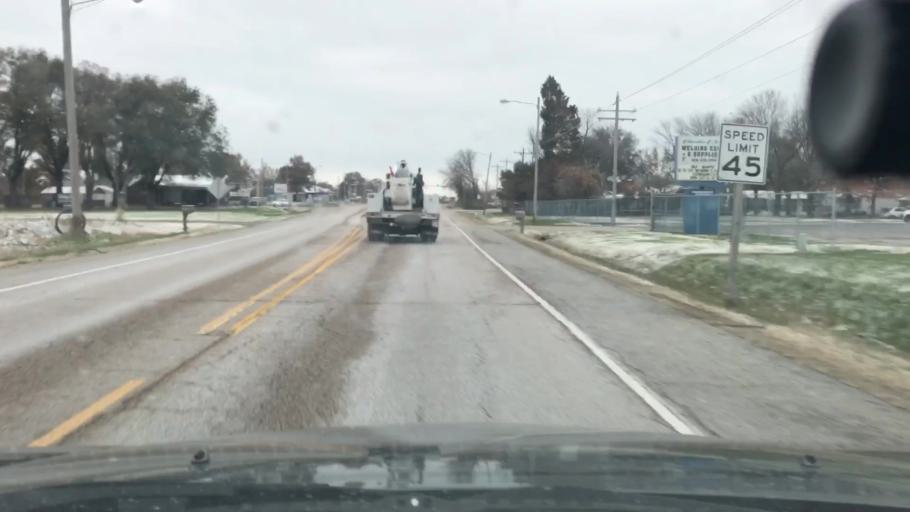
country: US
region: Illinois
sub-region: Madison County
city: Pontoon Beach
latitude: 38.7296
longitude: -90.0708
